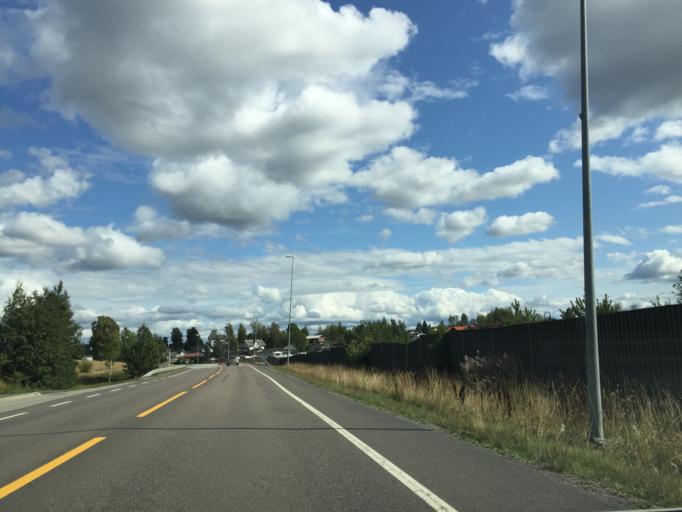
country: NO
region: Ostfold
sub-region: Spydeberg
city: Spydeberg
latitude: 59.6163
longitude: 11.0617
